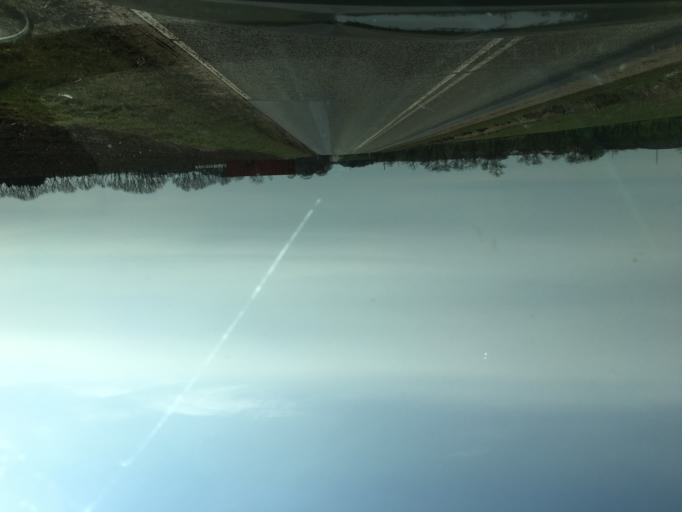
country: DK
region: South Denmark
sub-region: Kolding Kommune
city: Kolding
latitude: 55.5082
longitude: 9.3866
